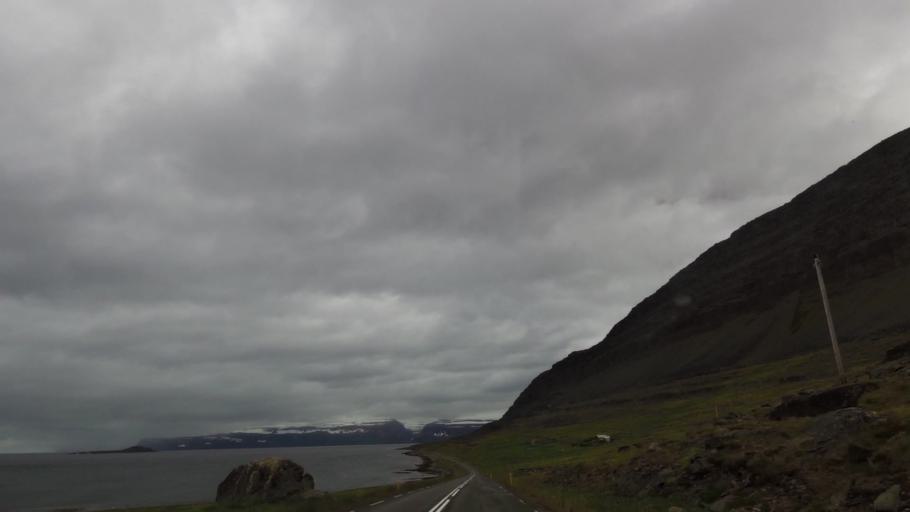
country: IS
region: Westfjords
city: Isafjoerdur
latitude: 66.0065
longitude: -22.7841
